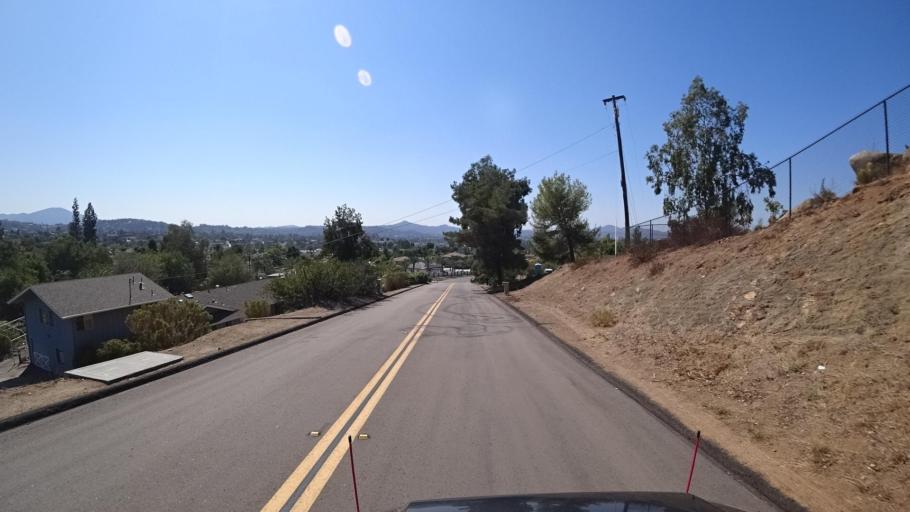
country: US
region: California
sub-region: San Diego County
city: Granite Hills
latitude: 32.8034
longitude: -116.8979
